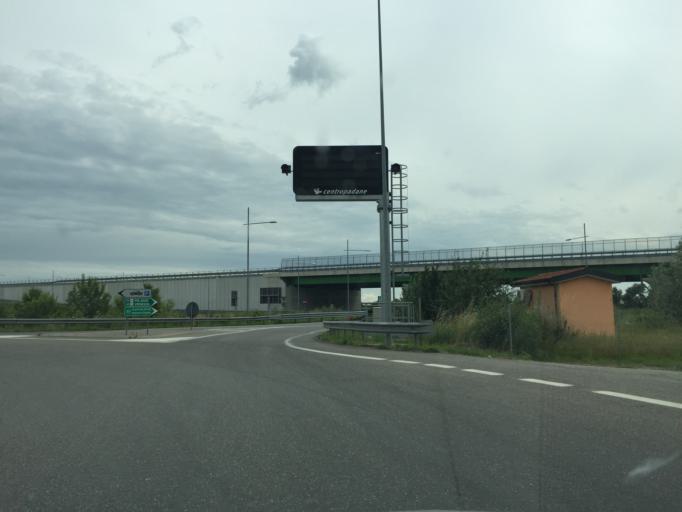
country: IT
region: Lombardy
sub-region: Provincia di Brescia
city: Montirone
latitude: 45.4662
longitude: 10.2145
